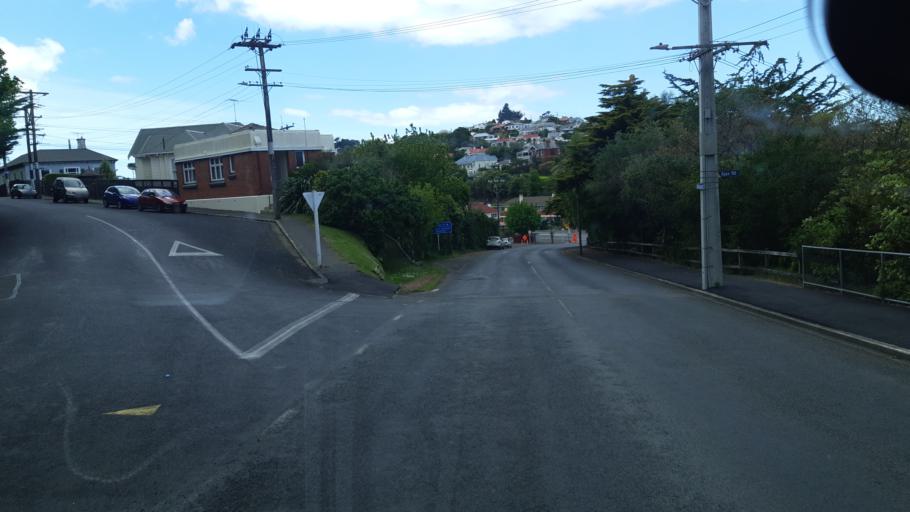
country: NZ
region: Otago
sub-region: Dunedin City
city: Portobello
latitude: -45.8176
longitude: 170.6167
